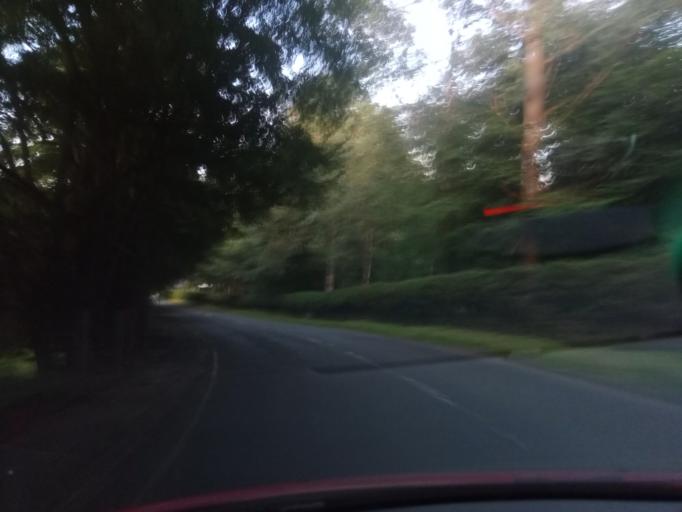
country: GB
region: England
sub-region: Northumberland
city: Bardon Mill
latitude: 54.9049
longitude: -2.3485
